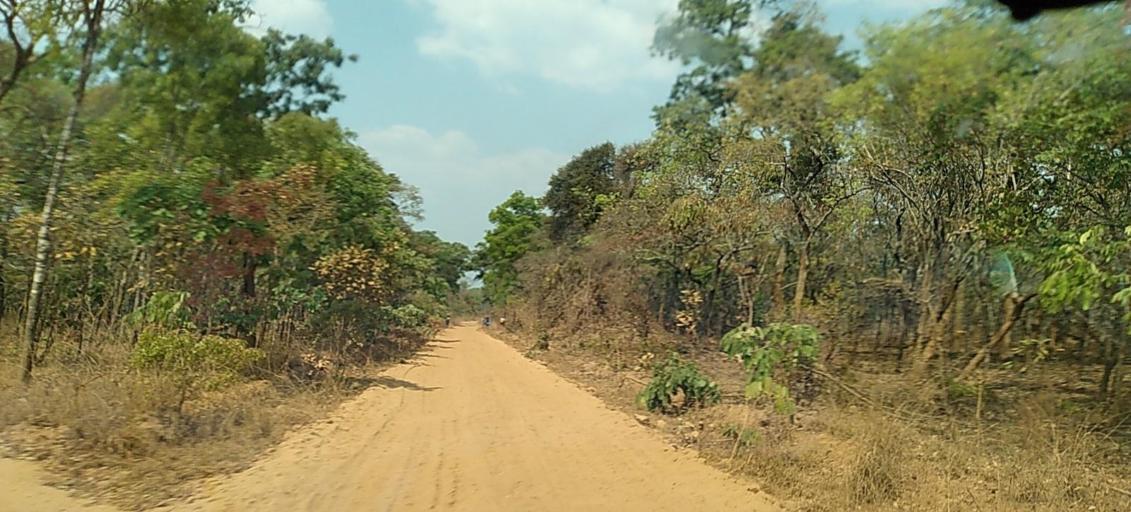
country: ZM
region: North-Western
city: Kasempa
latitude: -13.3209
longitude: 26.0427
